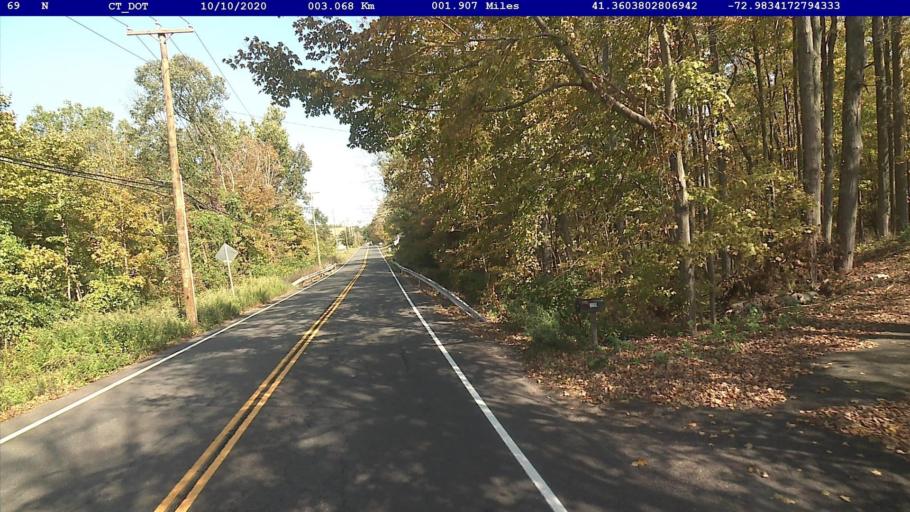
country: US
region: Connecticut
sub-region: New Haven County
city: Woodbridge
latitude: 41.3604
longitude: -72.9834
